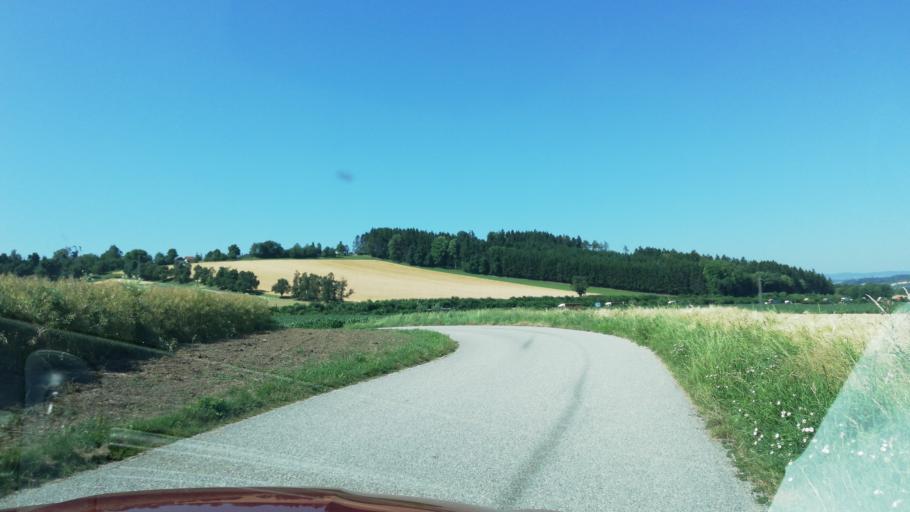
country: AT
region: Upper Austria
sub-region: Politischer Bezirk Grieskirchen
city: Bad Schallerbach
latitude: 48.1901
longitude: 13.9427
